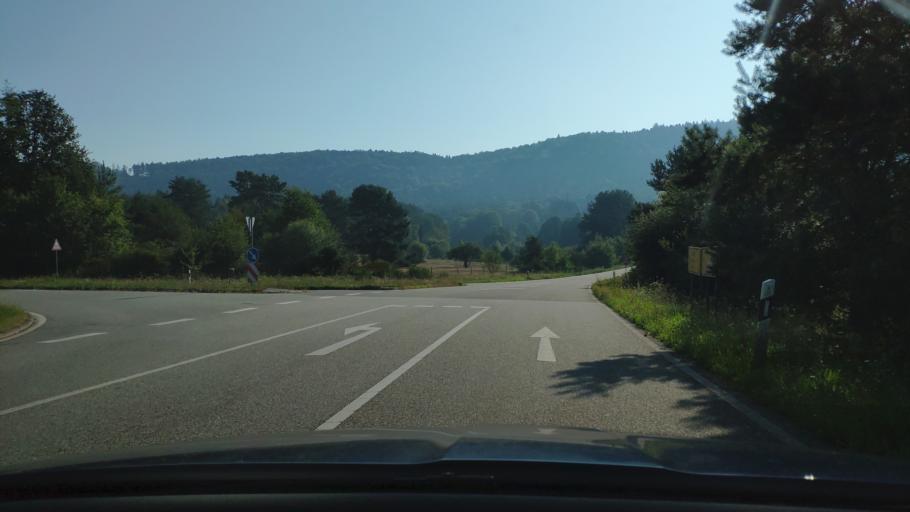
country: DE
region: Rheinland-Pfalz
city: Fischbach
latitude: 49.0702
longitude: 7.7065
